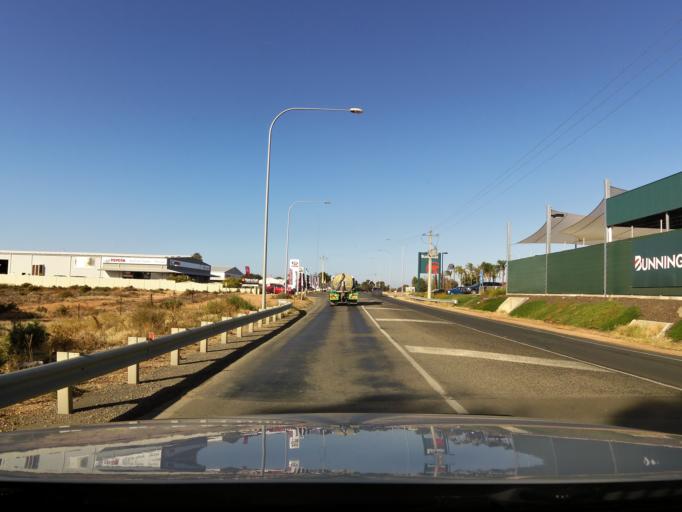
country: AU
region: South Australia
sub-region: Berri and Barmera
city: Berri
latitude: -34.2598
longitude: 140.6144
